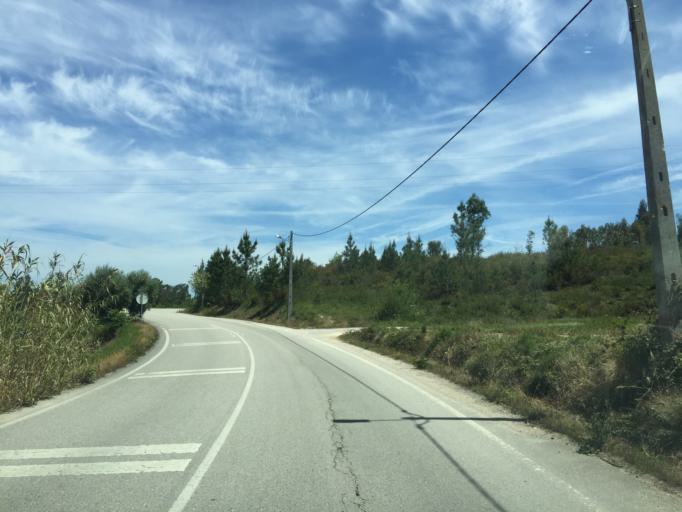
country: PT
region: Coimbra
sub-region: Soure
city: Soure
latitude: 40.0588
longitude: -8.6545
